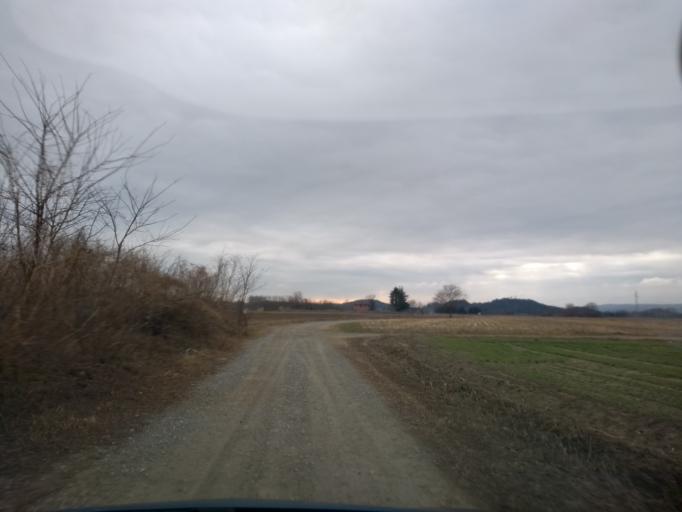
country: IT
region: Piedmont
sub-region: Provincia di Torino
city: Fiorano Canavese
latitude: 45.4852
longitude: 7.8410
